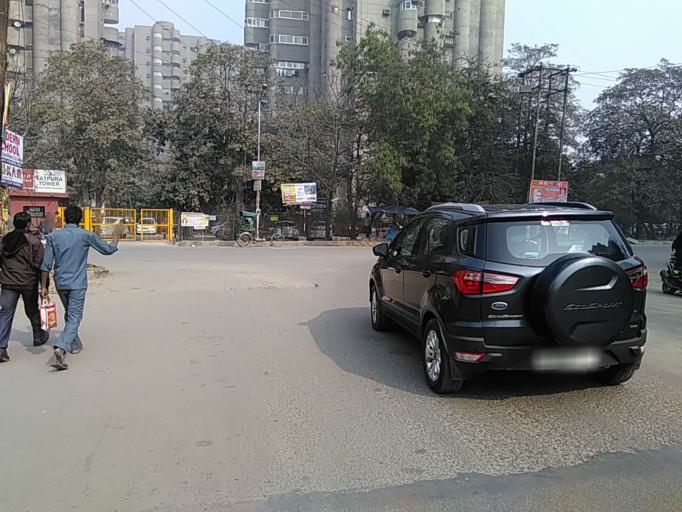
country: IN
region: Uttar Pradesh
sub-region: Gautam Buddha Nagar
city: Noida
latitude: 28.6430
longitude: 77.3194
